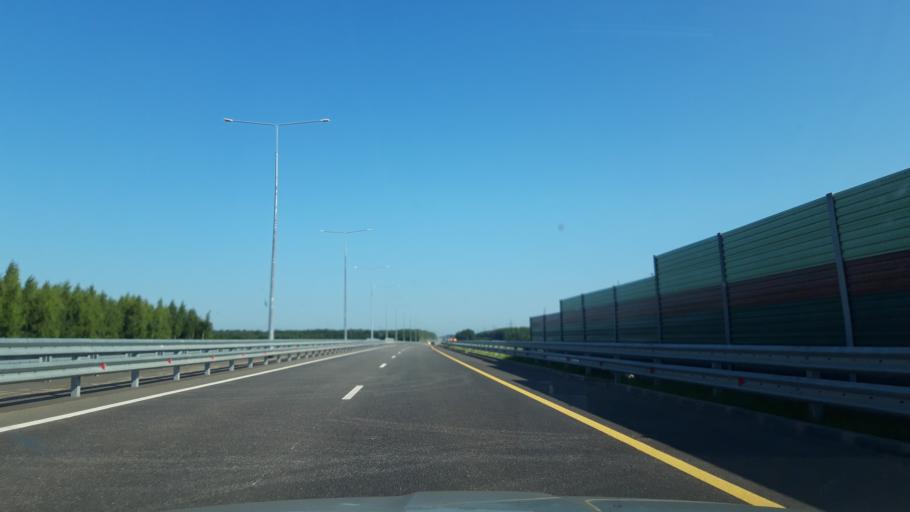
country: RU
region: Tverskaya
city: Zavidovo
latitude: 56.5217
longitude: 36.5021
